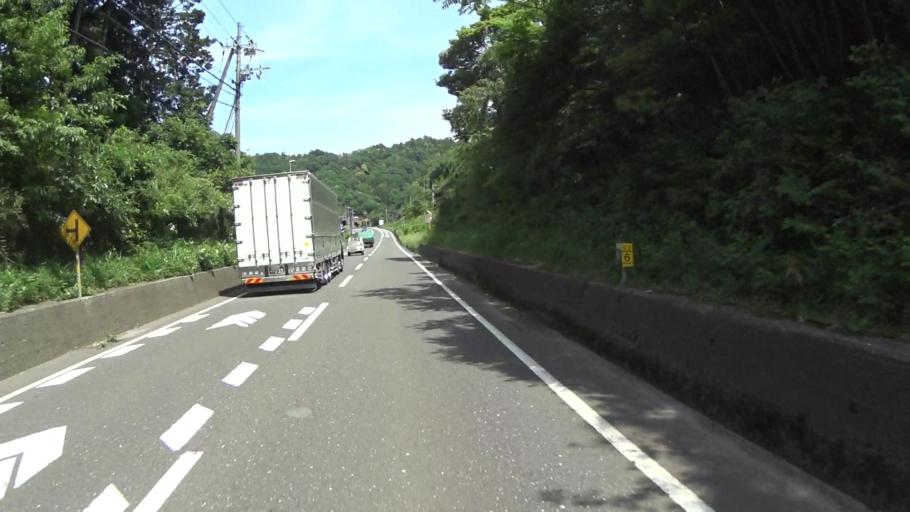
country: JP
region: Fukui
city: Obama
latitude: 35.4816
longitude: 135.6835
